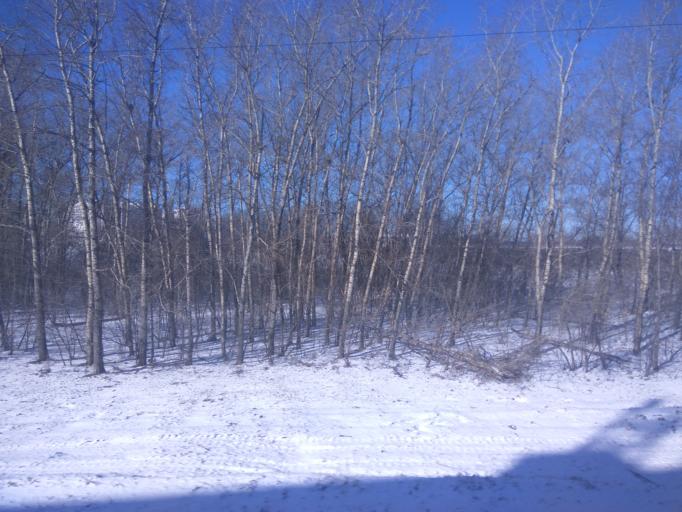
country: RU
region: Moscow
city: Tekstil'shchiki
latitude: 55.6971
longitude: 37.7310
